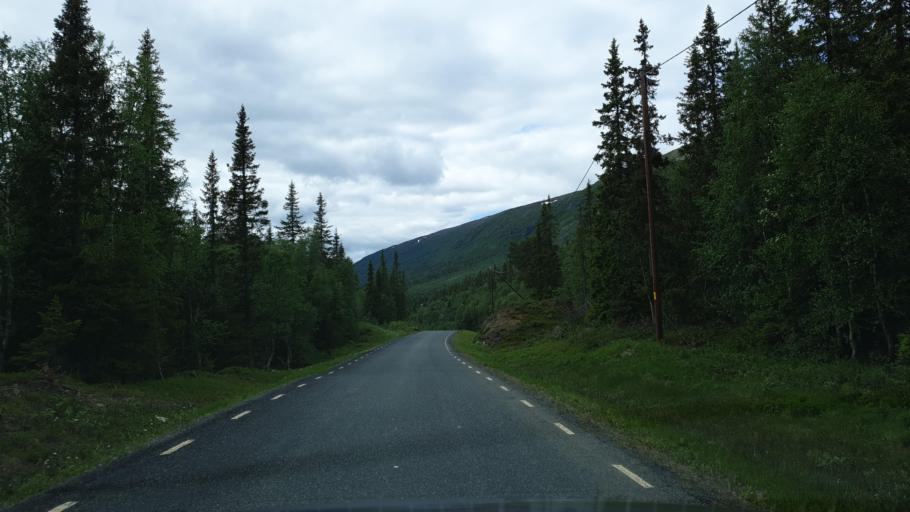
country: NO
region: Nordland
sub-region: Hattfjelldal
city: Hattfjelldal
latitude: 65.4306
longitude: 14.5917
